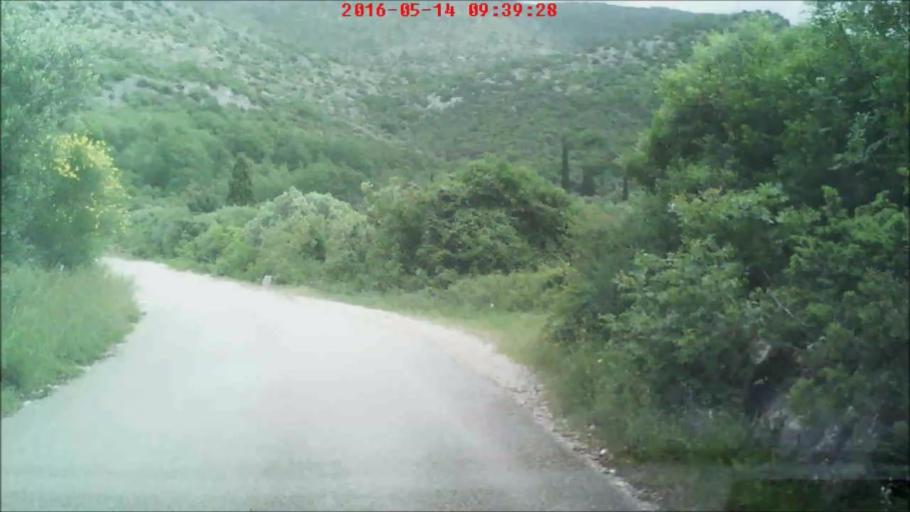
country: HR
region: Dubrovacko-Neretvanska
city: Podgora
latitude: 42.7904
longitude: 17.8914
